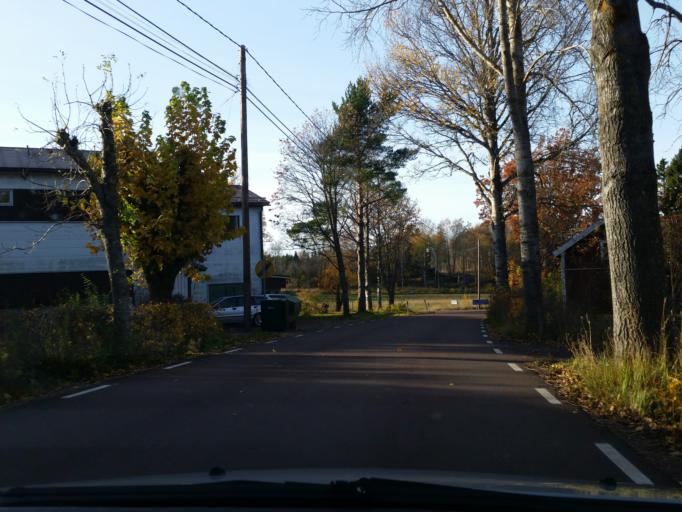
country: AX
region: Alands landsbygd
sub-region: Jomala
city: Jomala
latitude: 60.1425
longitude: 19.9726
